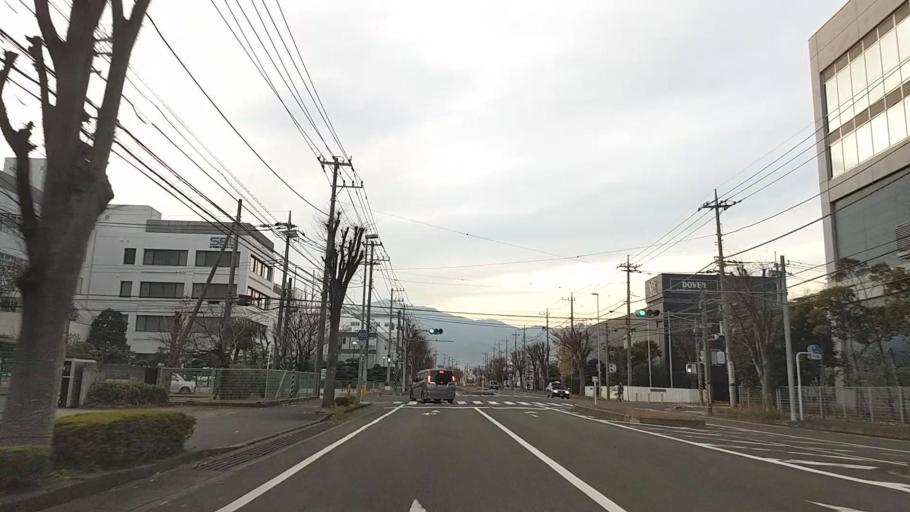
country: JP
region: Kanagawa
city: Atsugi
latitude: 35.4279
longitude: 139.3417
